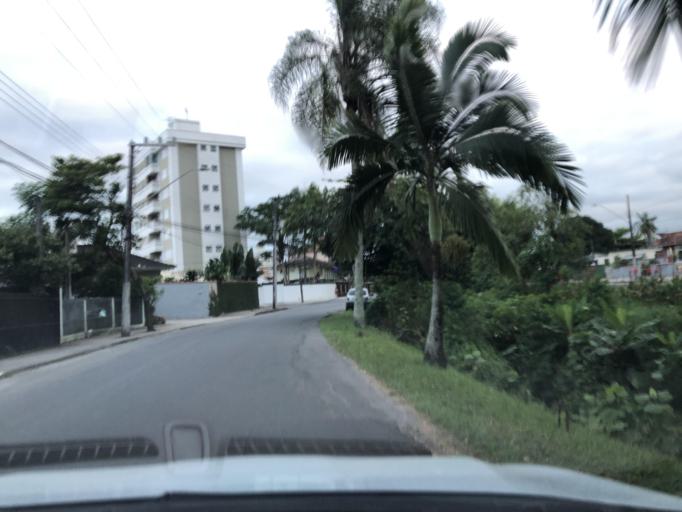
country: BR
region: Santa Catarina
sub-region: Joinville
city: Joinville
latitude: -26.2715
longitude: -48.8695
